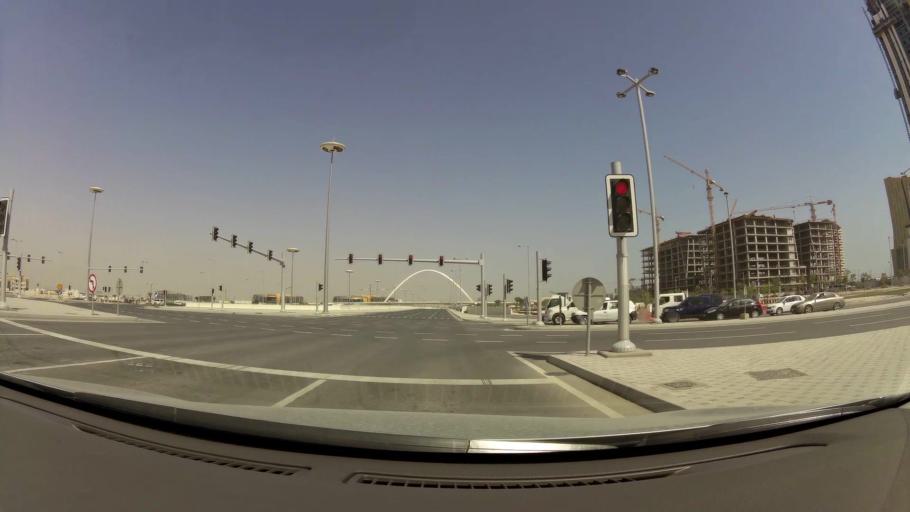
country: QA
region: Baladiyat ad Dawhah
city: Doha
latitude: 25.3934
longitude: 51.5174
